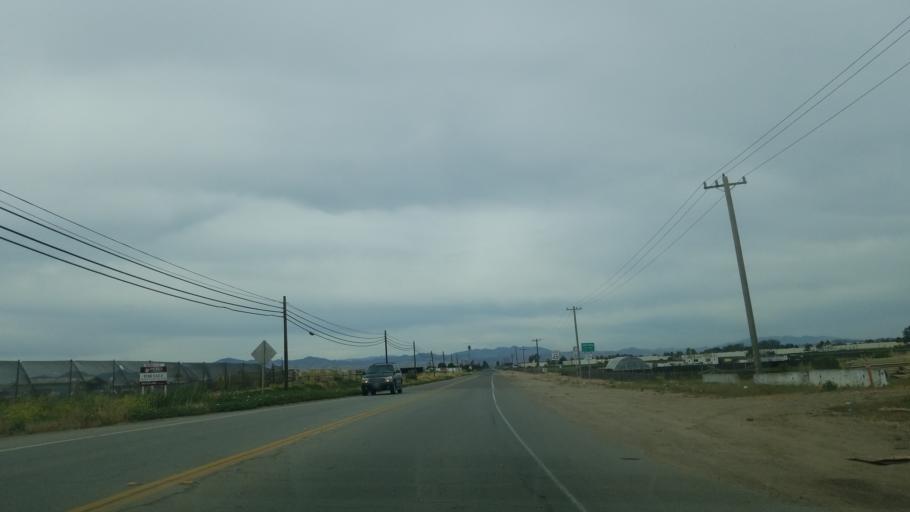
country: US
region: California
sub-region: Santa Barbara County
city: Santa Maria
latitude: 34.9208
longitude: -120.4734
